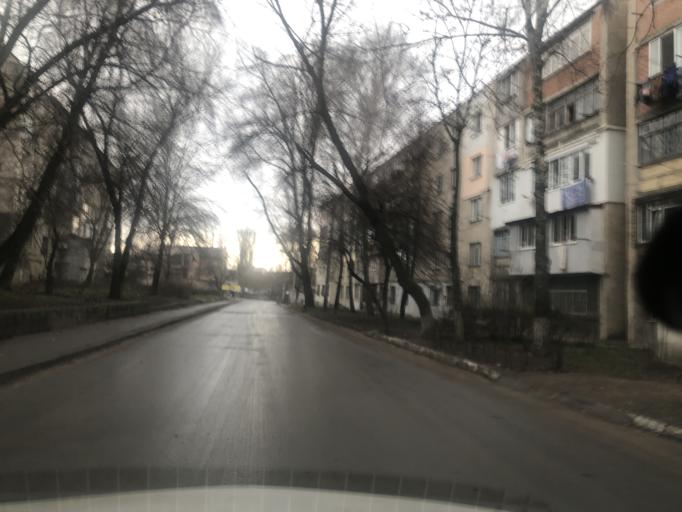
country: MD
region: Chisinau
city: Stauceni
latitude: 47.0634
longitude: 28.8484
